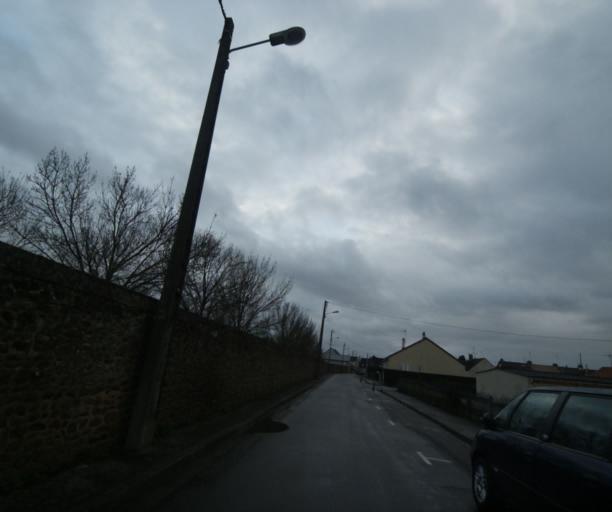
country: FR
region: Pays de la Loire
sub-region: Departement de la Sarthe
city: Coulaines
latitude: 48.0205
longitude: 0.1886
